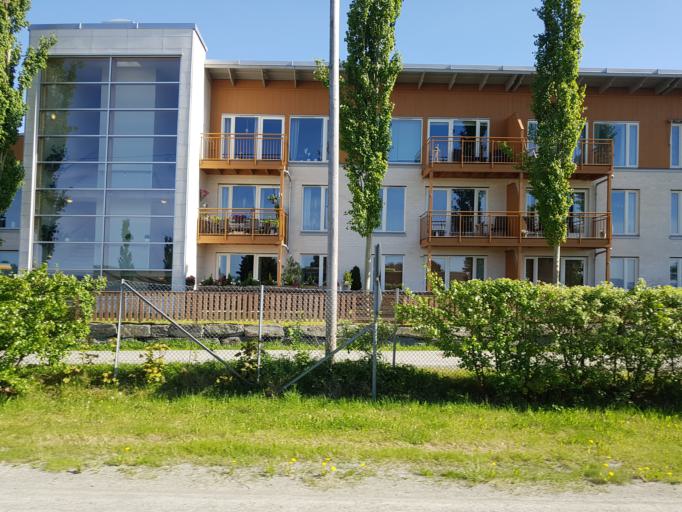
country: NO
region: Sor-Trondelag
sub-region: Malvik
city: Malvik
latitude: 63.4400
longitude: 10.6377
